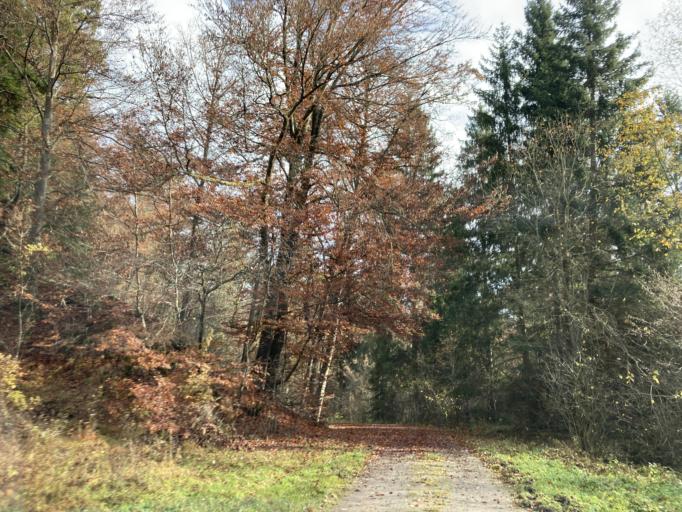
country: DE
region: Baden-Wuerttemberg
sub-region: Regierungsbezirk Stuttgart
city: Bondorf
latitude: 48.4777
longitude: 8.8301
